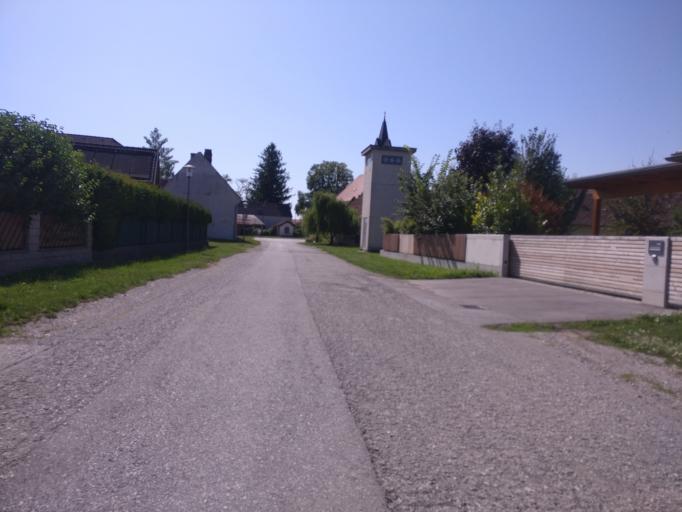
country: AT
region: Lower Austria
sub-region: Politischer Bezirk Wiener Neustadt
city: Ebenfurth
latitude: 47.9033
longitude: 16.3525
